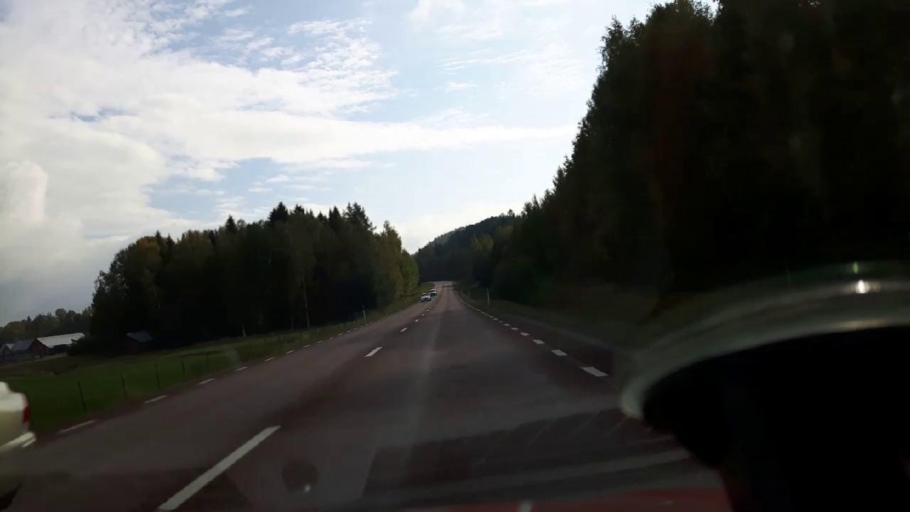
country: SE
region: Gaevleborg
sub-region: Bollnas Kommun
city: Kilafors
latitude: 61.2092
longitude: 16.7424
